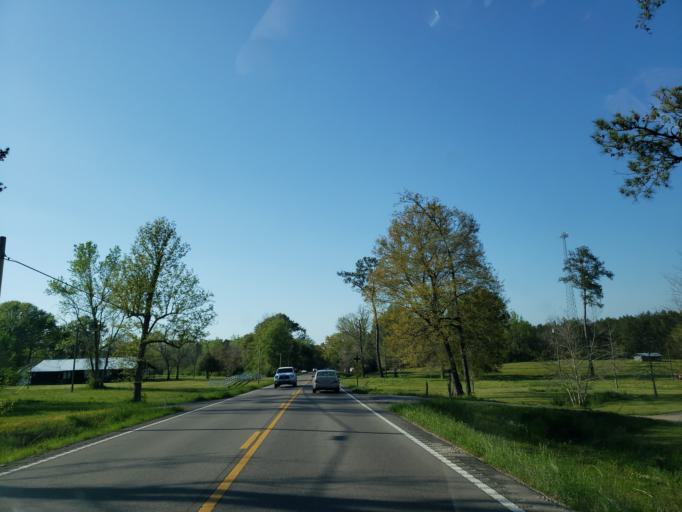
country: US
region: Mississippi
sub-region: Jones County
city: Laurel
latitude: 31.6245
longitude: -89.0886
